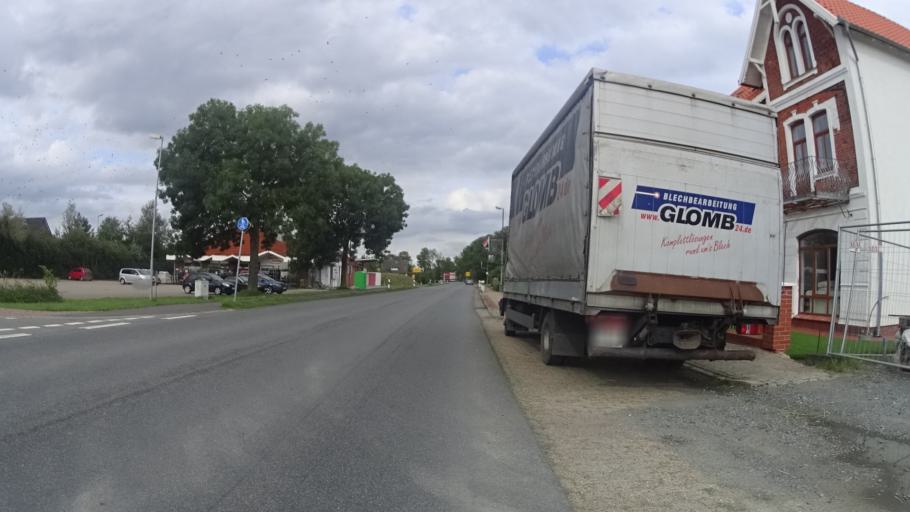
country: DE
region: Lower Saxony
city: Wischhafen
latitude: 53.7790
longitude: 9.3229
